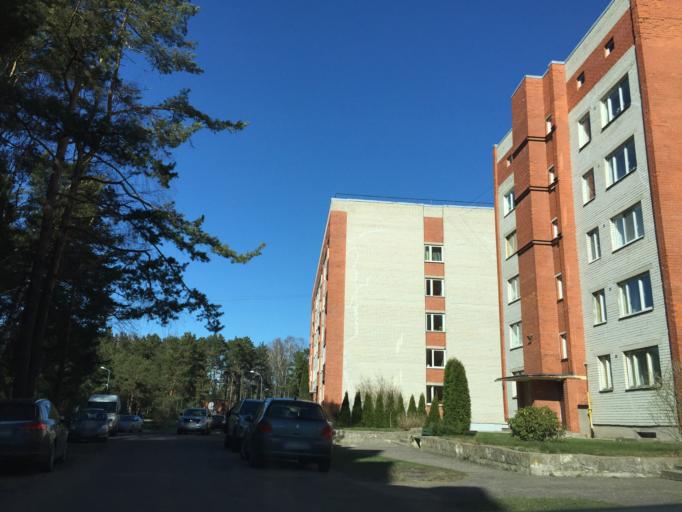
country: LV
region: Babite
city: Pinki
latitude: 56.9943
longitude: 23.9219
